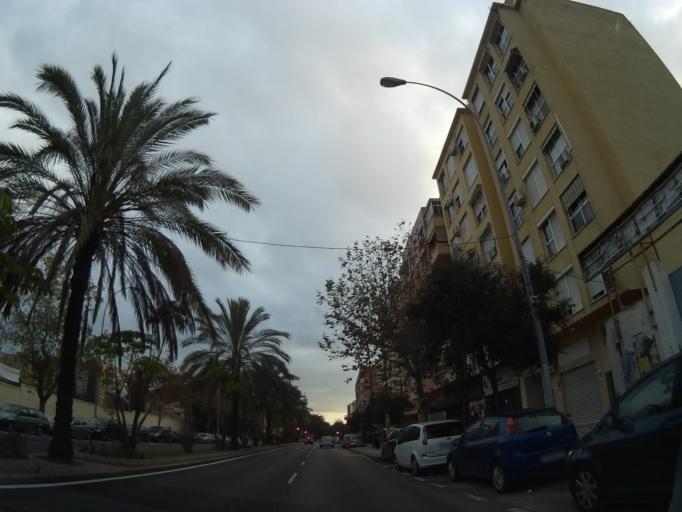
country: ES
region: Andalusia
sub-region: Provincia de Malaga
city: Malaga
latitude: 36.7101
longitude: -4.4526
